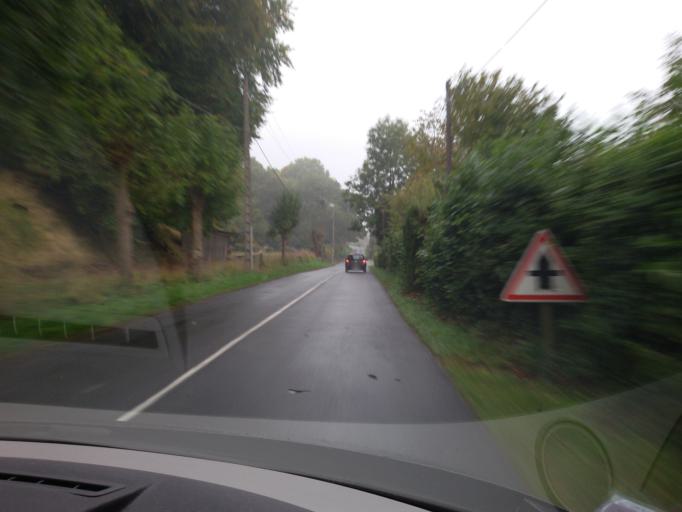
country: FR
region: Lower Normandy
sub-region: Departement du Calvados
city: Ablon
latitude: 49.4226
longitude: 0.3225
